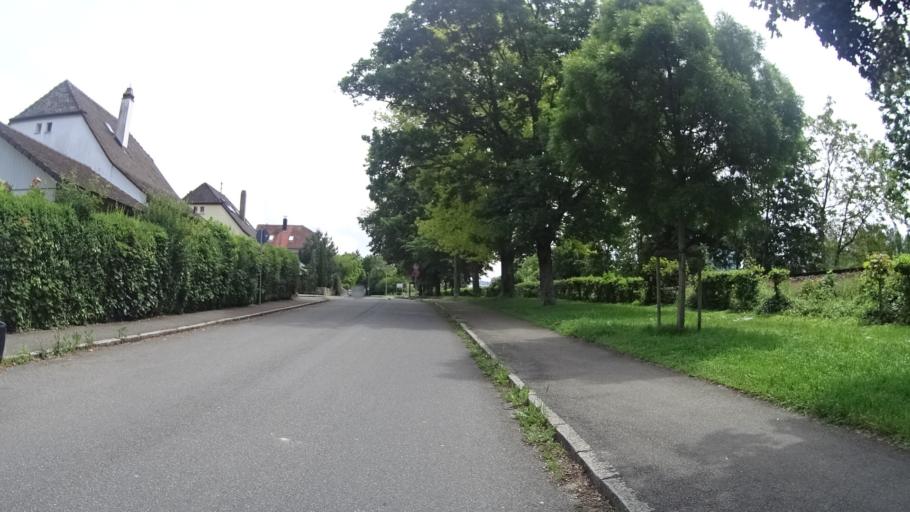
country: CH
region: Basel-City
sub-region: Basel-Stadt
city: Bettingen
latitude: 47.5530
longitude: 7.6511
